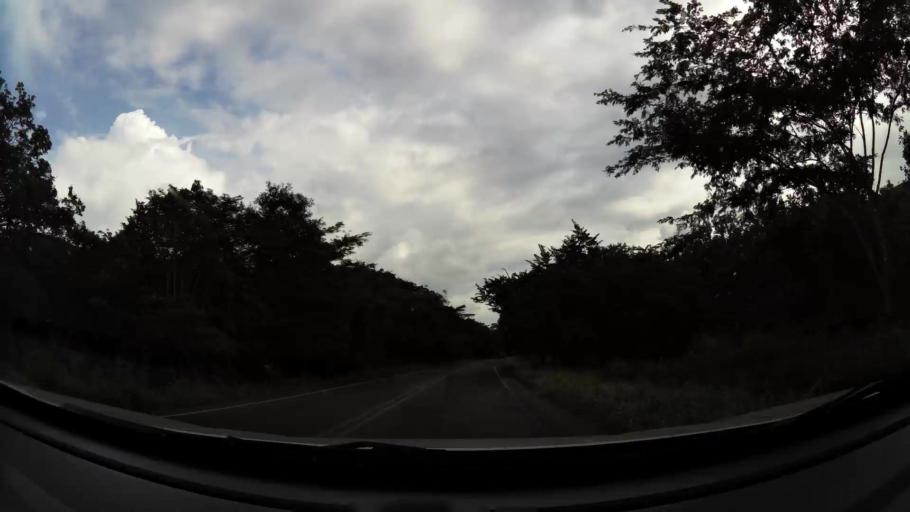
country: CR
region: Guanacaste
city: Juntas
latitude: 10.2338
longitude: -84.9820
